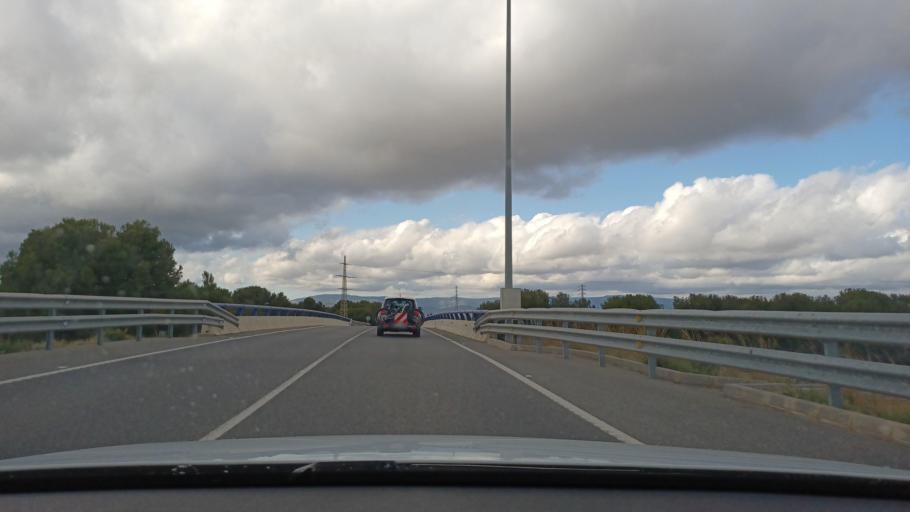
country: ES
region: Catalonia
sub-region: Provincia de Tarragona
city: Cambrils
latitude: 41.0811
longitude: 1.0410
